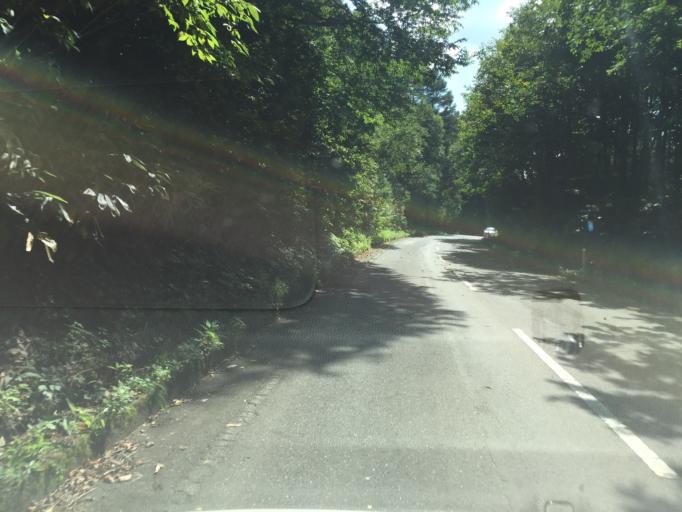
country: JP
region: Fukushima
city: Inawashiro
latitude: 37.6630
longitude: 140.1427
